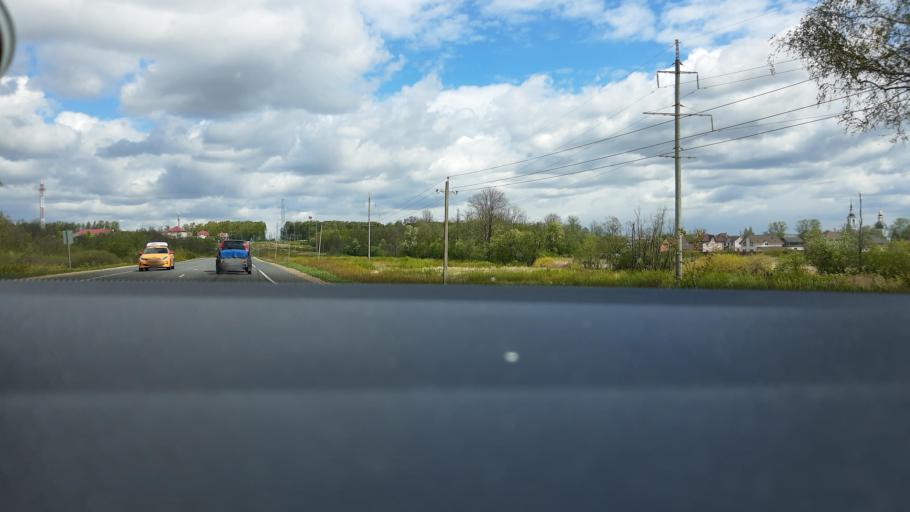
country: RU
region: Moskovskaya
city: Dmitrov
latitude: 56.3505
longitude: 37.4860
